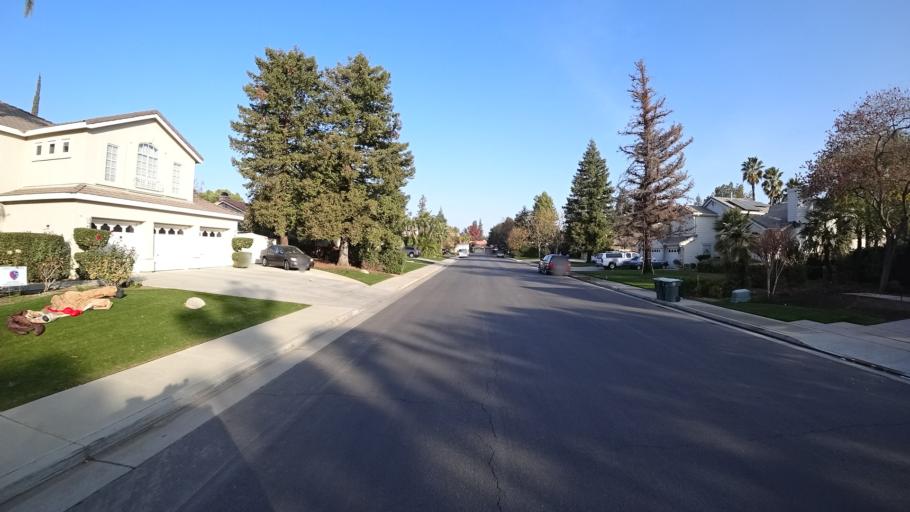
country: US
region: California
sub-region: Kern County
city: Rosedale
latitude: 35.3707
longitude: -119.1424
